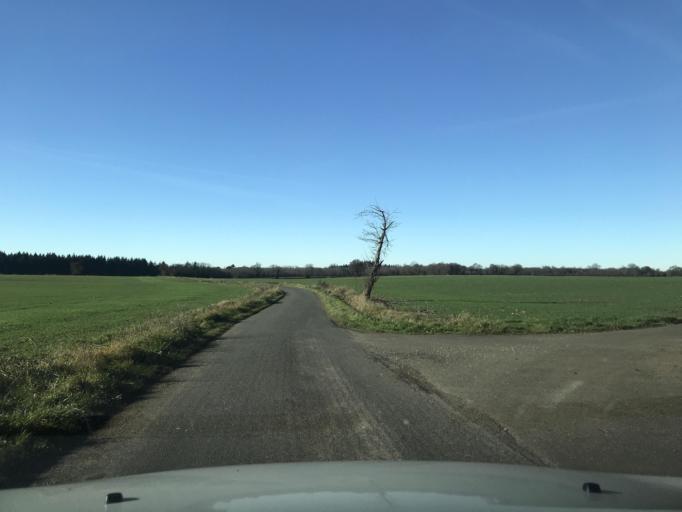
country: FR
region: Poitou-Charentes
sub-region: Departement de la Charente
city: Saint-Claud
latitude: 45.8537
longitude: 0.4973
